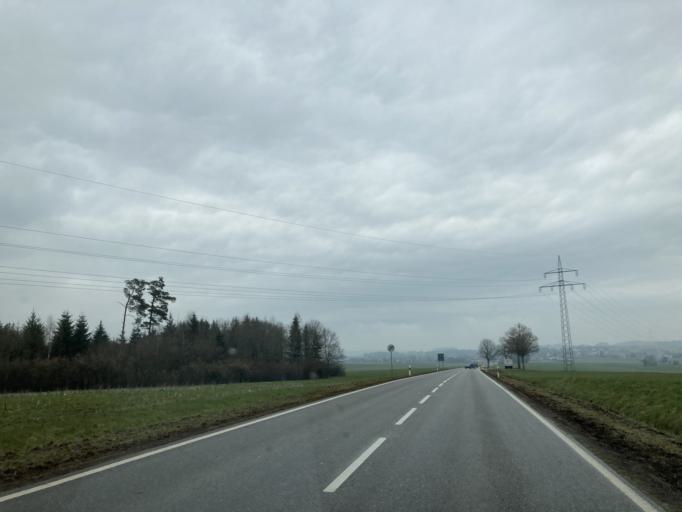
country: DE
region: Baden-Wuerttemberg
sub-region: Freiburg Region
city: Seedorf
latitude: 48.2607
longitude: 8.4608
